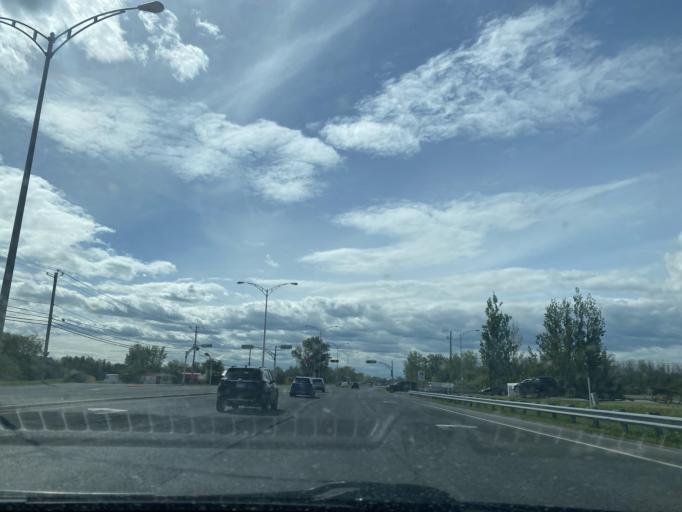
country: CA
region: Quebec
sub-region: Monteregie
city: Carignan
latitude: 45.4621
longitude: -73.3307
